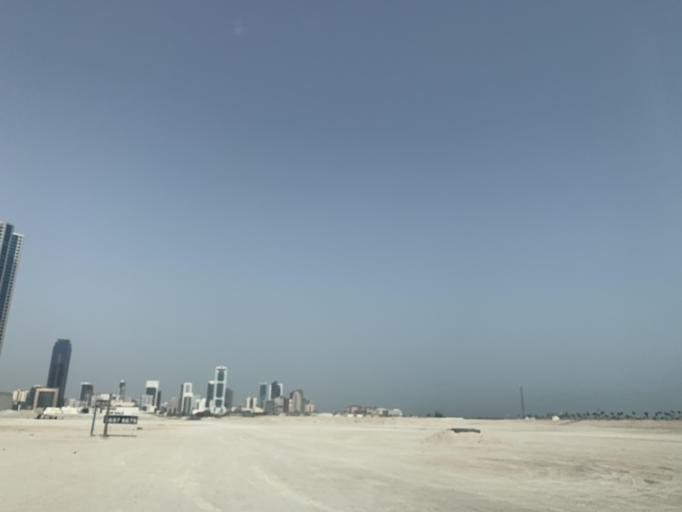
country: BH
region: Manama
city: Jidd Hafs
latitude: 26.2387
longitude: 50.5556
